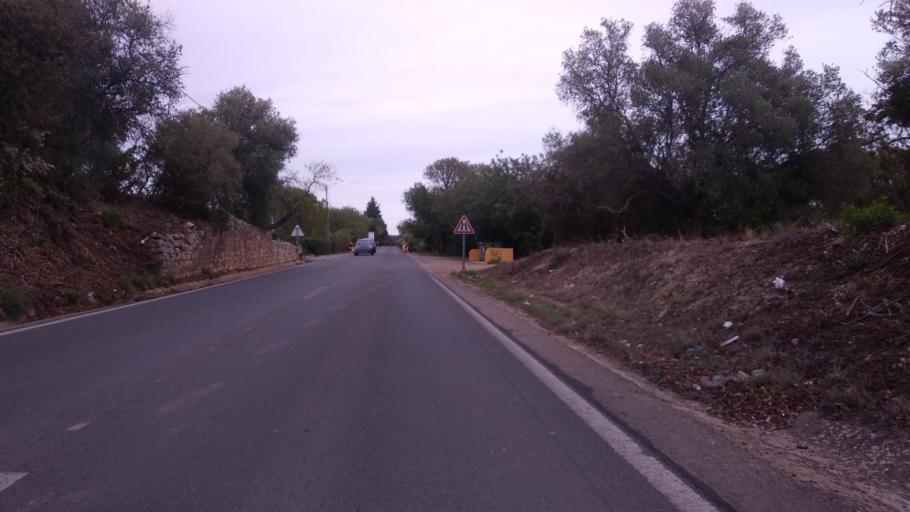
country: PT
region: Faro
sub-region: Faro
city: Santa Barbara de Nexe
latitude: 37.1470
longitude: -7.9662
